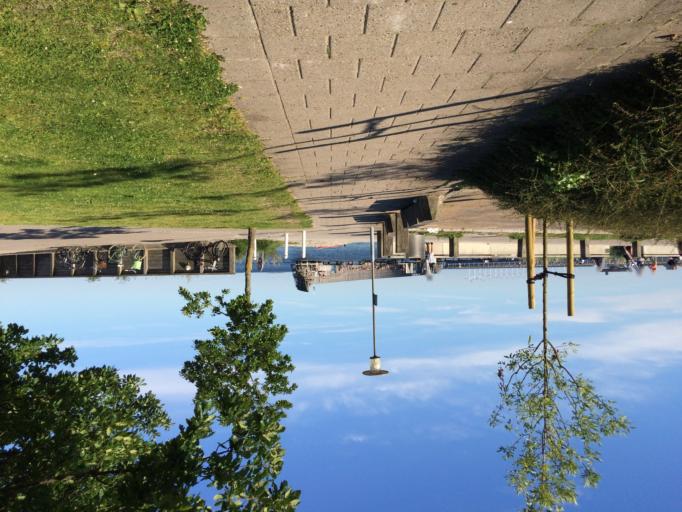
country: DK
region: Capital Region
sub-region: Tarnby Kommune
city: Tarnby
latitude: 55.6442
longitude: 12.6482
